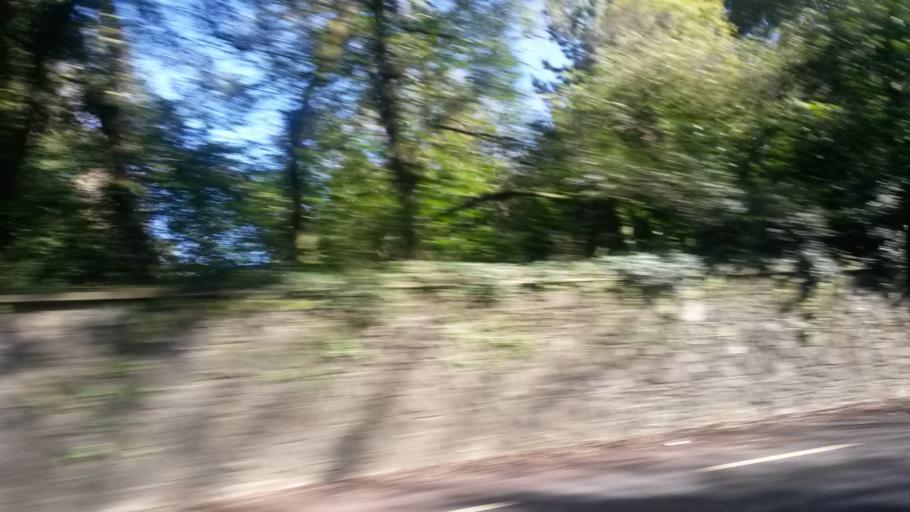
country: IE
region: Munster
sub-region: County Cork
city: Cobh
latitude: 51.8913
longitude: -8.3014
